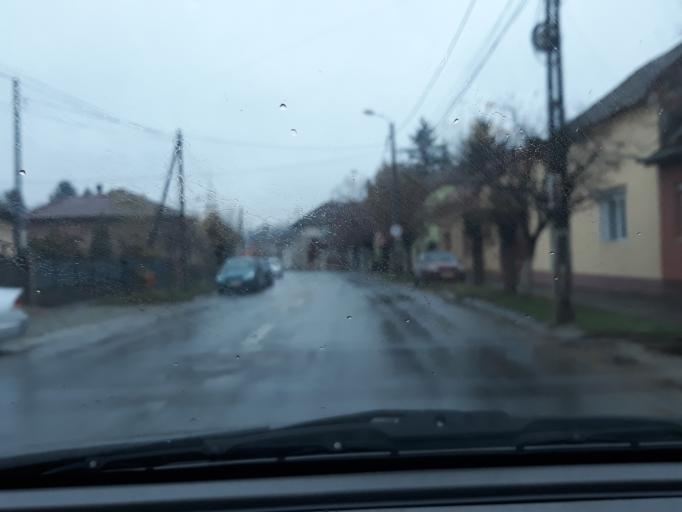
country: RO
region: Bihor
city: Margita
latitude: 47.3495
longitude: 22.3398
